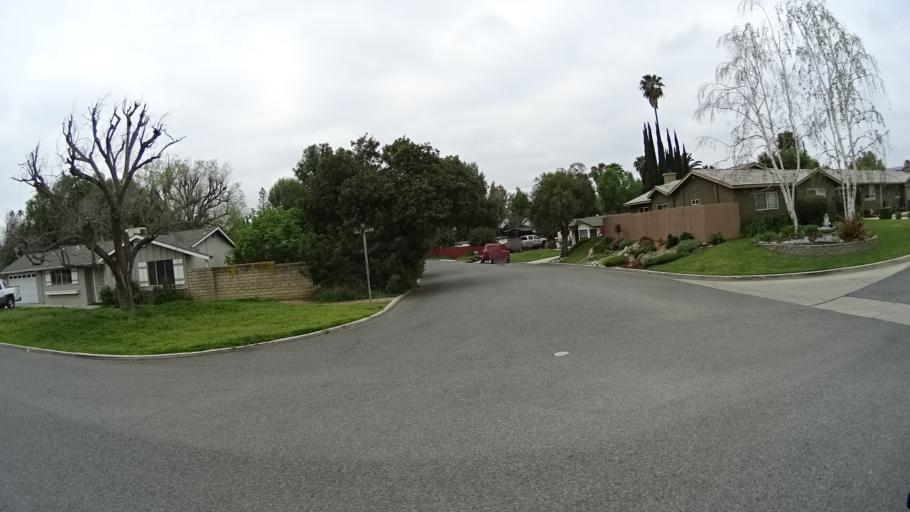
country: US
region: California
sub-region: Ventura County
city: Thousand Oaks
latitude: 34.2065
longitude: -118.8650
